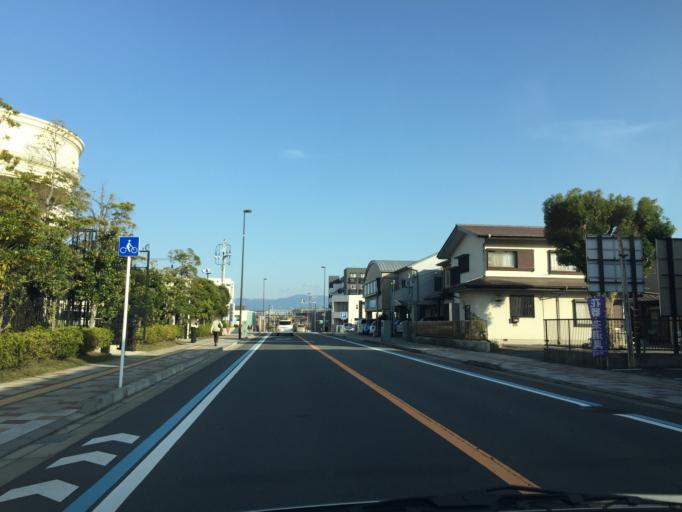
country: JP
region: Shizuoka
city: Numazu
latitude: 35.1054
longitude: 138.8629
